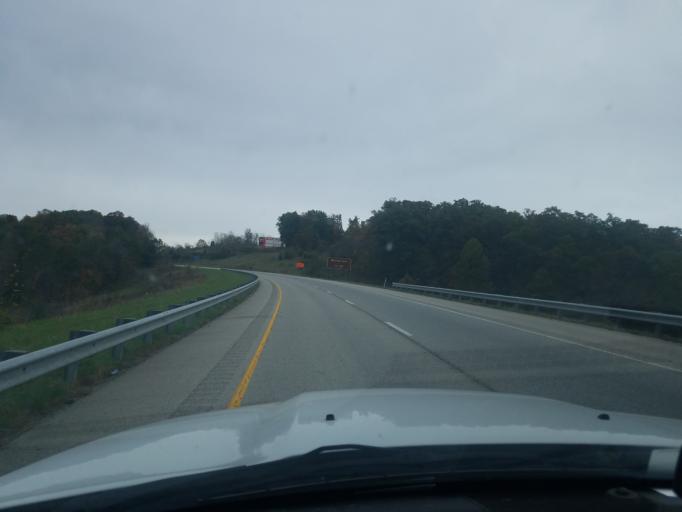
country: US
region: Indiana
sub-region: Crawford County
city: English
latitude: 38.2356
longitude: -86.3731
